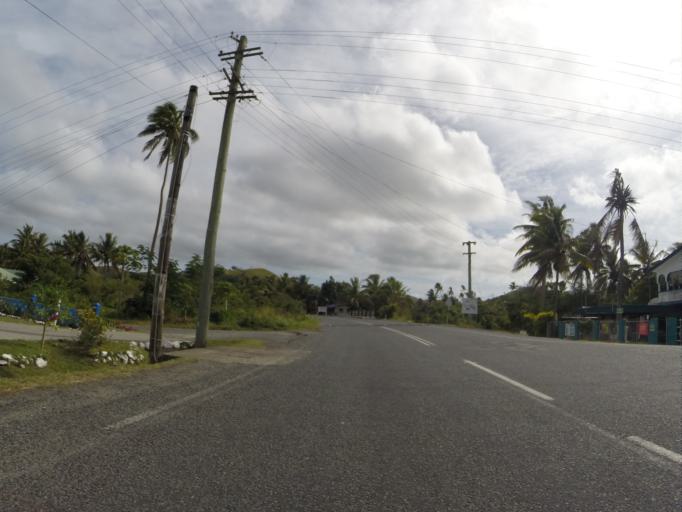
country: FJ
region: Western
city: Nadi
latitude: -18.1718
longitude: 177.5417
